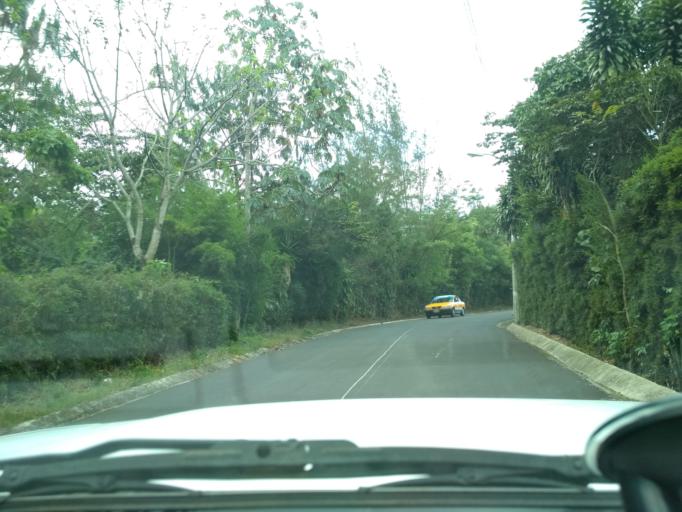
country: MX
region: Veracruz
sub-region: Cordoba
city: San Jose de Abajo [Unidad Habitacional]
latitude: 18.9230
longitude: -96.9572
